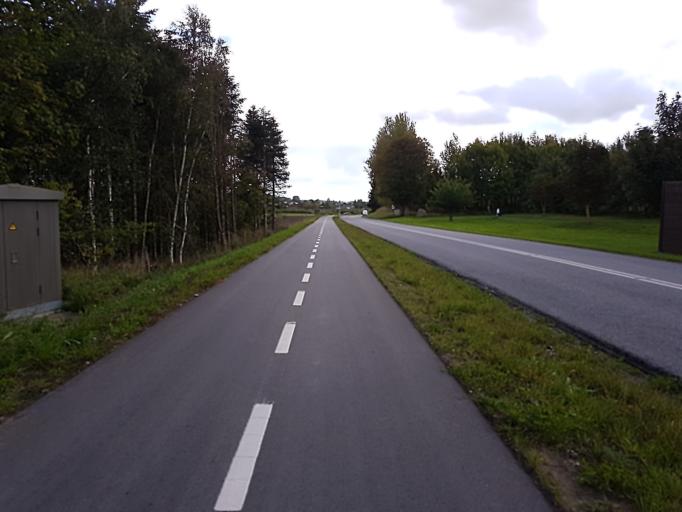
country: DK
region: Zealand
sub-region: Roskilde Kommune
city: Gundsomagle
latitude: 55.7467
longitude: 12.1429
